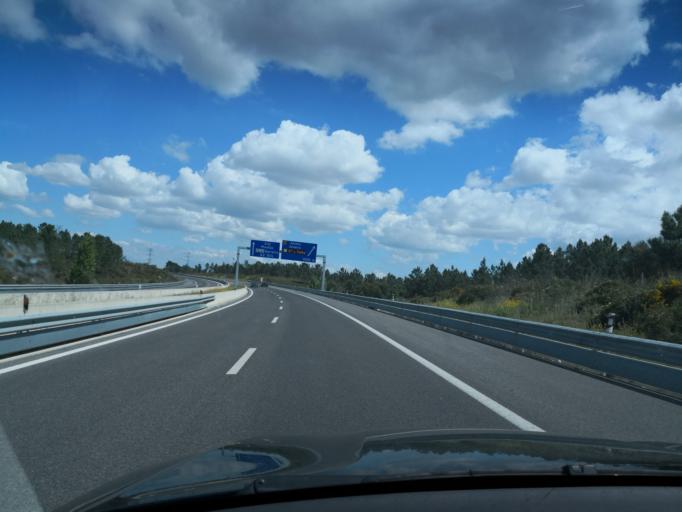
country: PT
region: Setubal
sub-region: Seixal
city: Corroios
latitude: 38.6065
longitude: -9.1466
